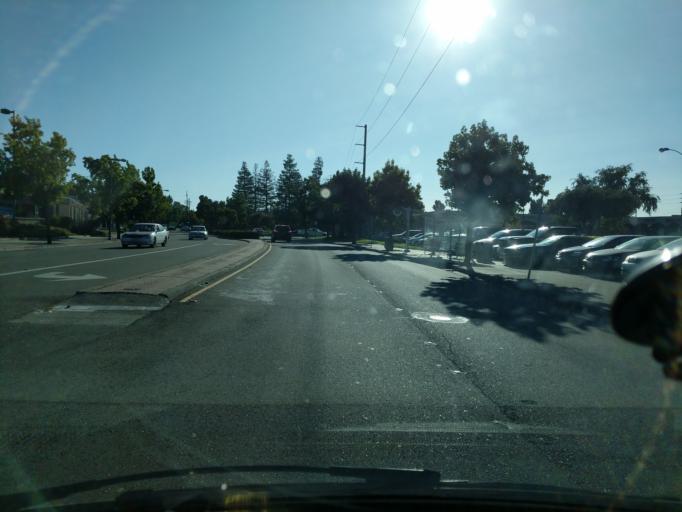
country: US
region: California
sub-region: Alameda County
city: Livermore
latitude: 37.6808
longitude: -121.7785
